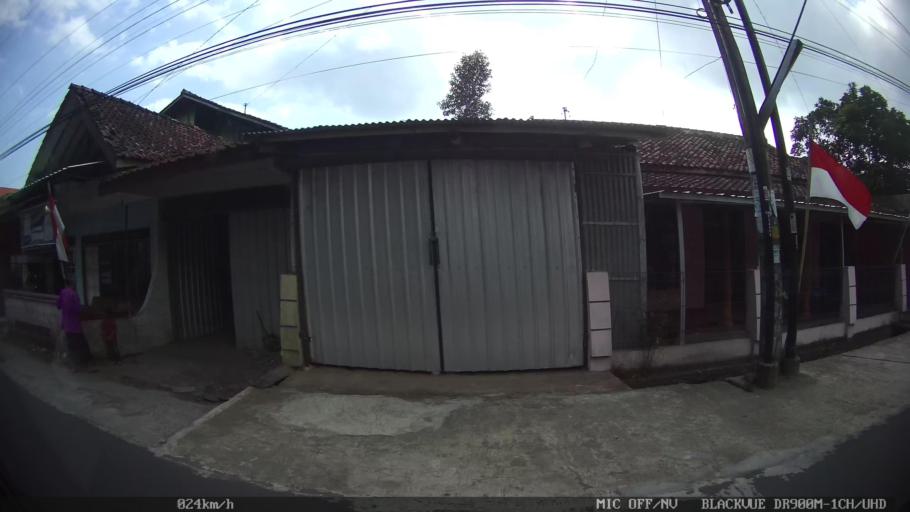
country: ID
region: Daerah Istimewa Yogyakarta
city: Gamping Lor
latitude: -7.7908
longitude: 110.3367
